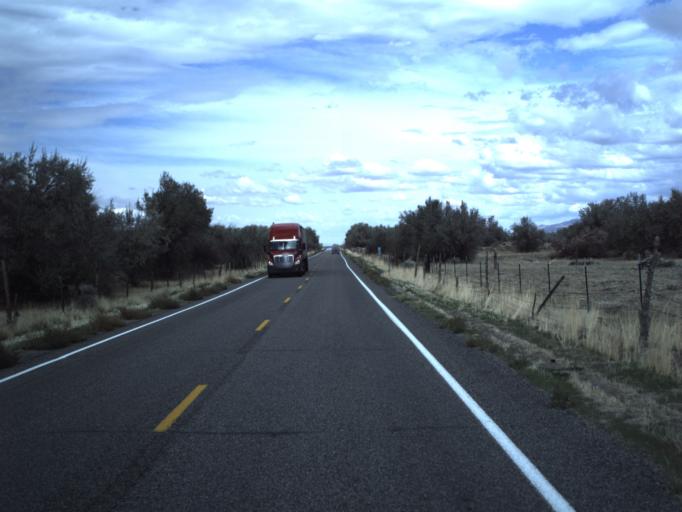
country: US
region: Utah
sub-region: Millard County
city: Fillmore
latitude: 39.0843
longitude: -112.4099
